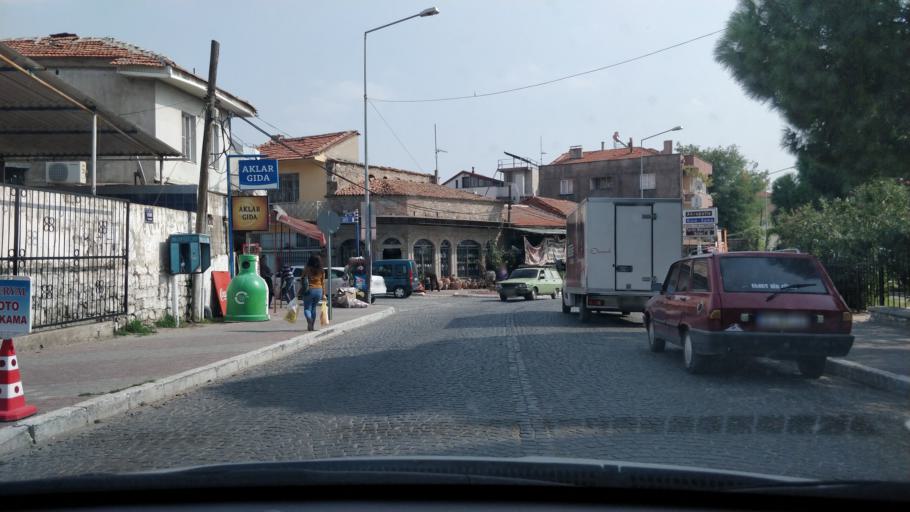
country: TR
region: Izmir
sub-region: Bergama
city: Bergama
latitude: 39.1223
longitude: 27.1837
